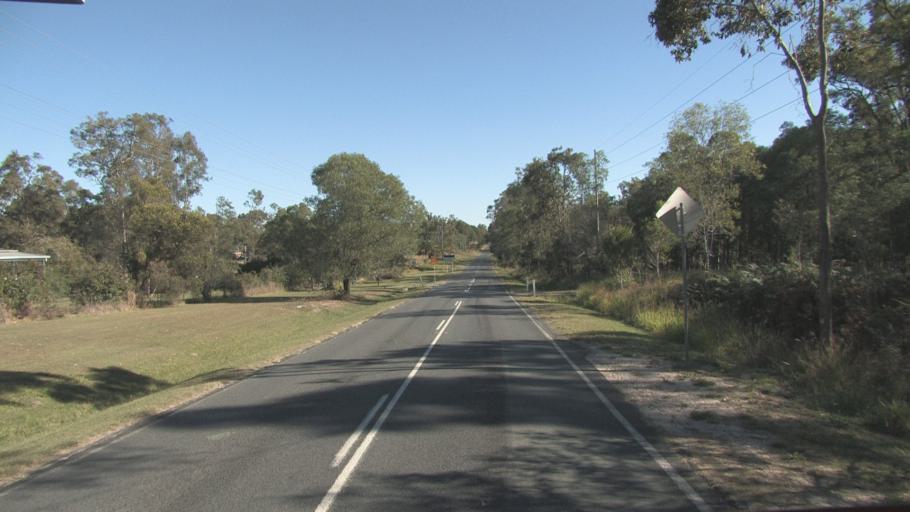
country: AU
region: Queensland
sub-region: Logan
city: North Maclean
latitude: -27.7840
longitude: 153.0516
